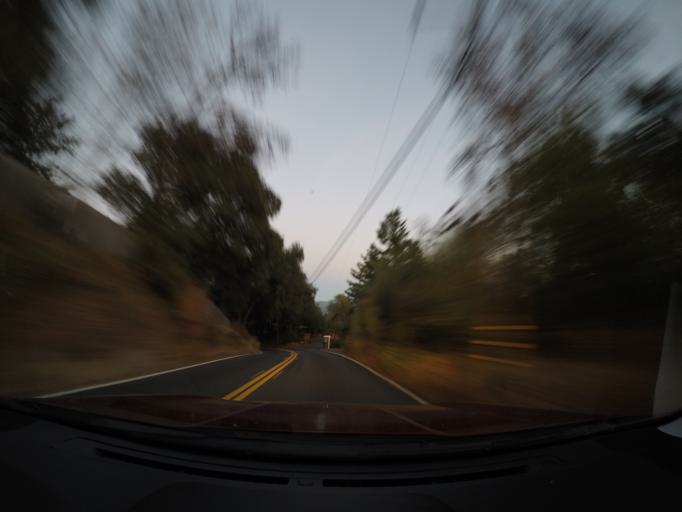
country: US
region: California
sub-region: Santa Clara County
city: Lexington Hills
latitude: 37.1438
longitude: -121.9894
